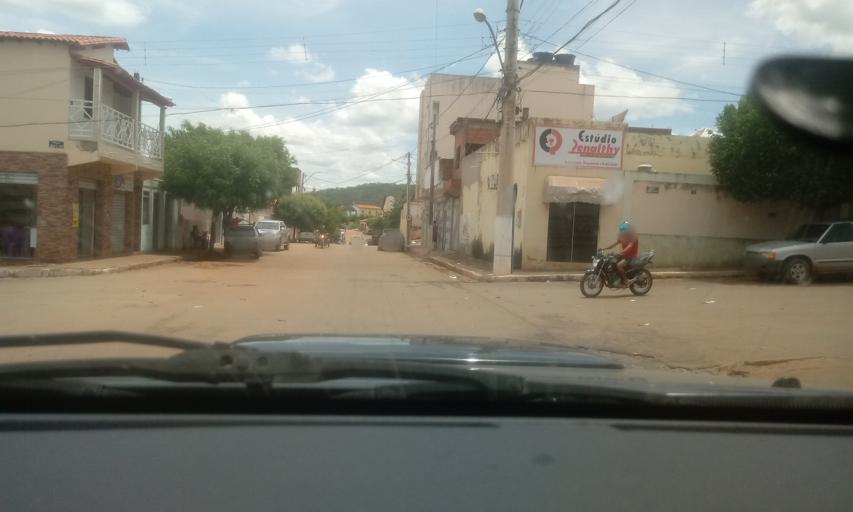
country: BR
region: Bahia
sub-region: Riacho De Santana
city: Riacho de Santana
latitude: -13.6087
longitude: -42.9378
